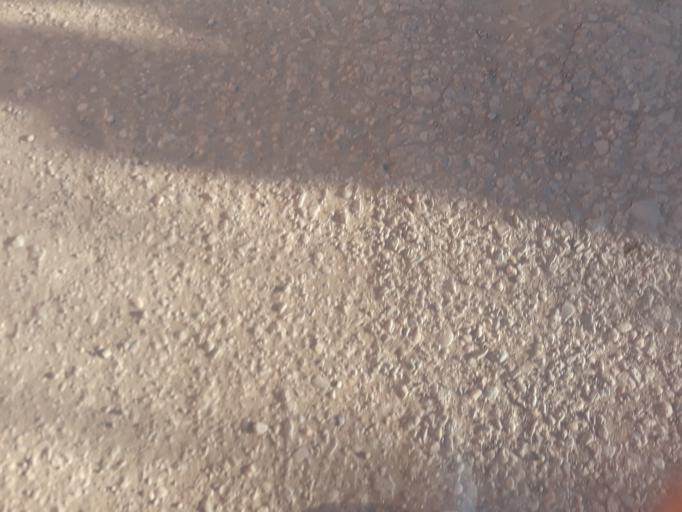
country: BO
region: La Paz
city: Achacachi
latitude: -16.0475
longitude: -68.6871
